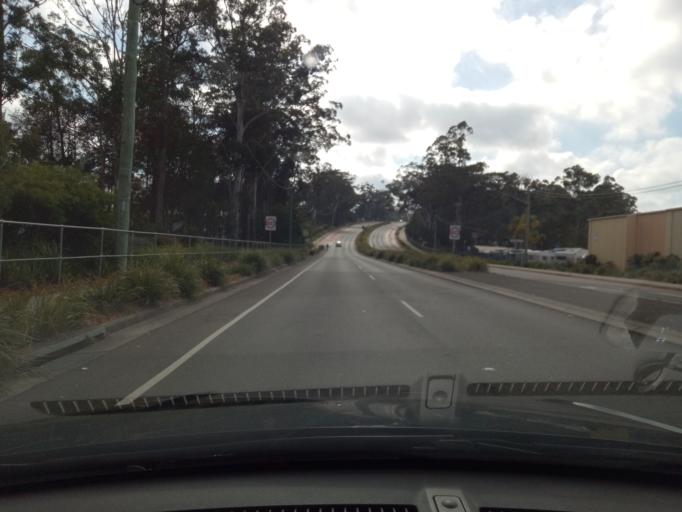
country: AU
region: New South Wales
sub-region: Gosford Shire
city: Erina
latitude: -33.4273
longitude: 151.3954
